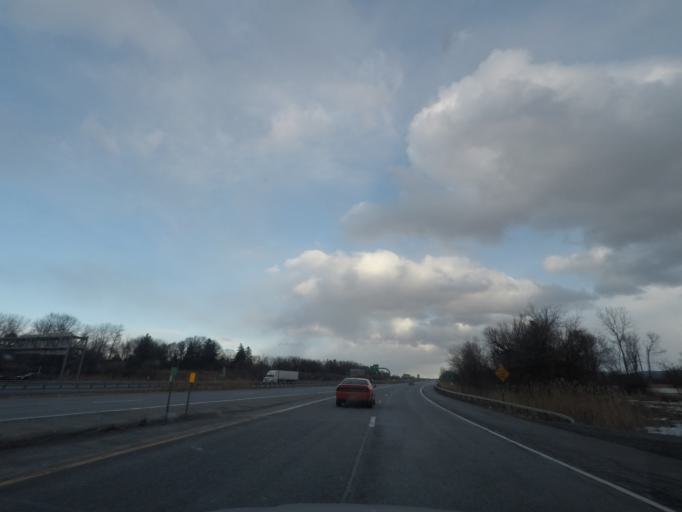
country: US
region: New York
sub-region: Oneida County
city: Utica
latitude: 43.1198
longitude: -75.2260
